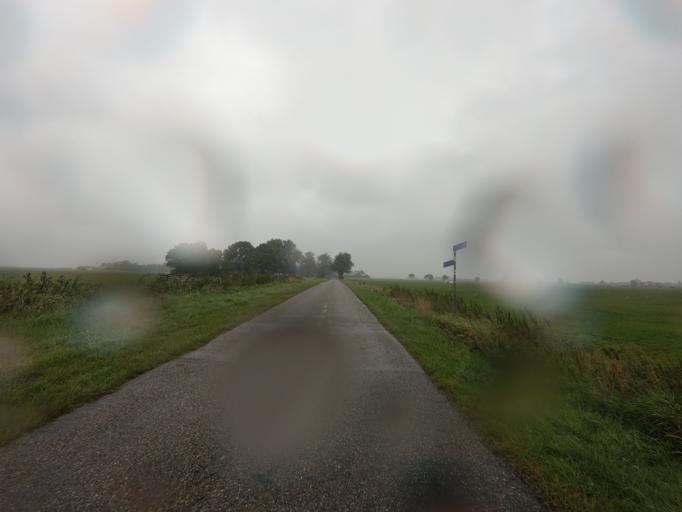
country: NL
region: Friesland
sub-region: Gemeente Boarnsterhim
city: Aldeboarn
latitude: 53.0680
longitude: 5.9246
